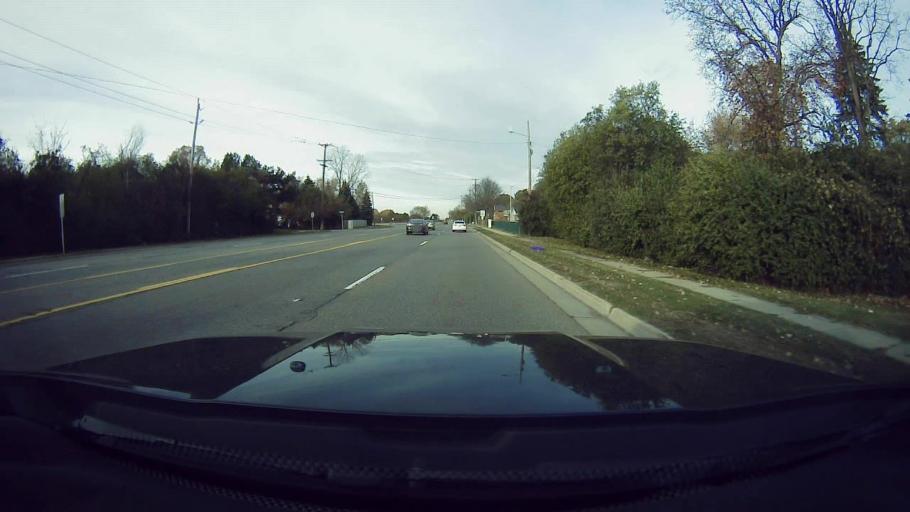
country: US
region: Michigan
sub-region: Oakland County
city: Lathrup Village
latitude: 42.4884
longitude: -83.2092
